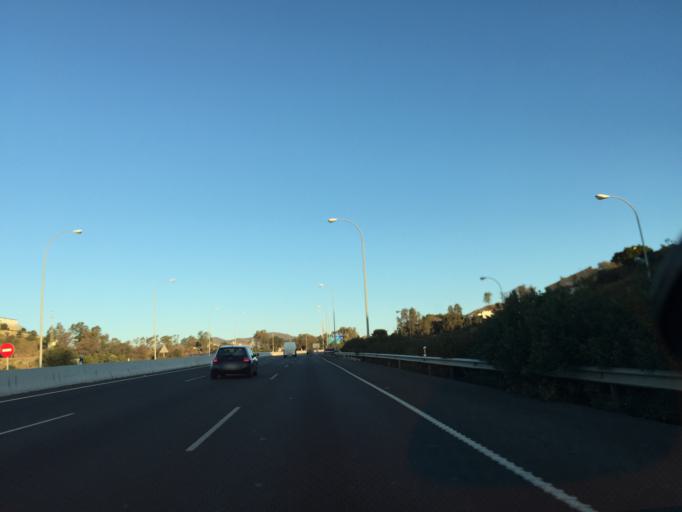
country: ES
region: Andalusia
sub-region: Provincia de Malaga
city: Malaga
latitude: 36.7421
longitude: -4.4034
